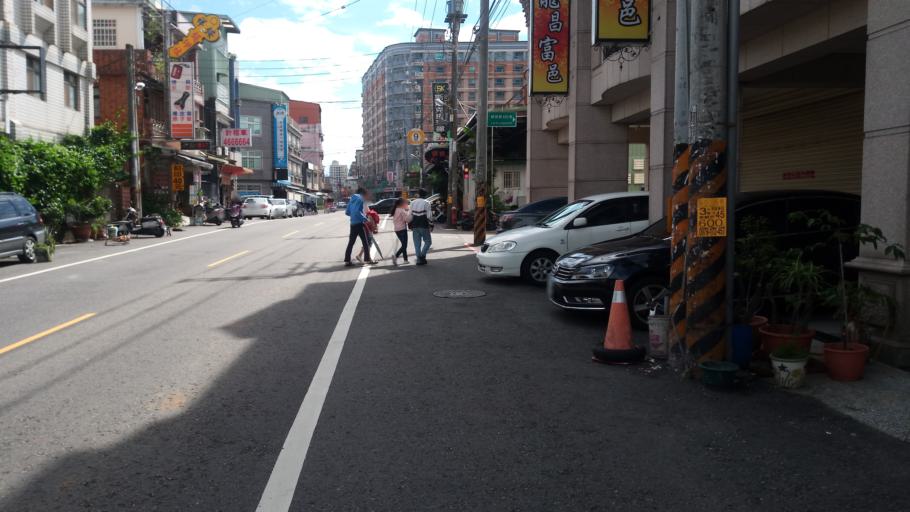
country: TW
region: Taiwan
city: Daxi
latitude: 24.9398
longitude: 121.2497
